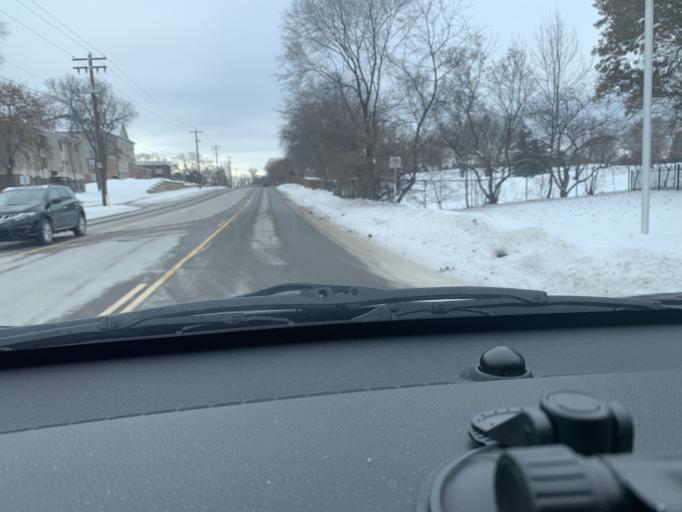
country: US
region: Minnesota
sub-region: Dakota County
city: South Saint Paul
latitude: 44.8888
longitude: -93.0703
